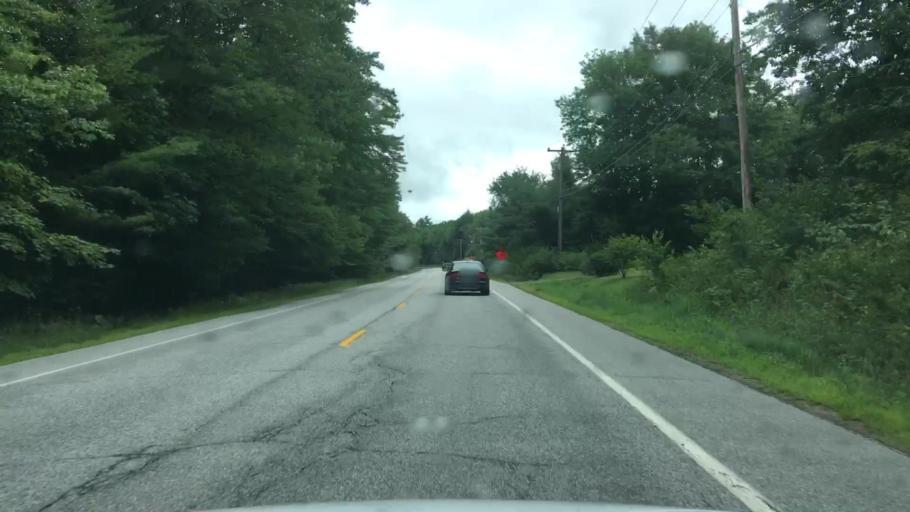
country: US
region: Maine
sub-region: York County
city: Cornish
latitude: 43.8221
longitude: -70.7724
